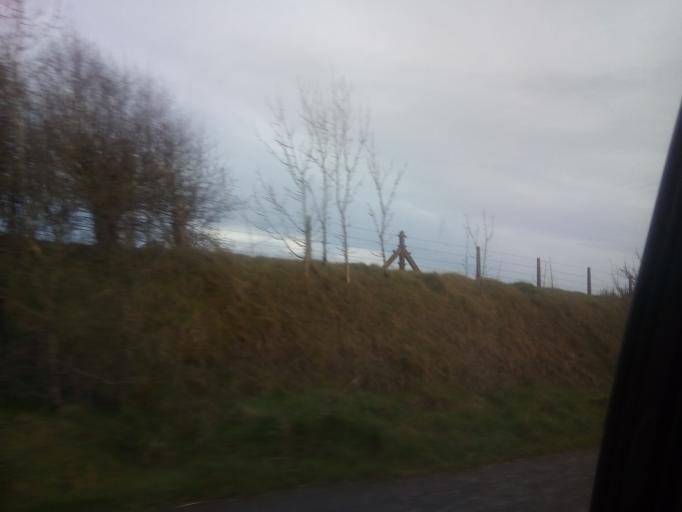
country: IE
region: Leinster
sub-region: Laois
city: Abbeyleix
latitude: 52.8533
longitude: -7.3879
